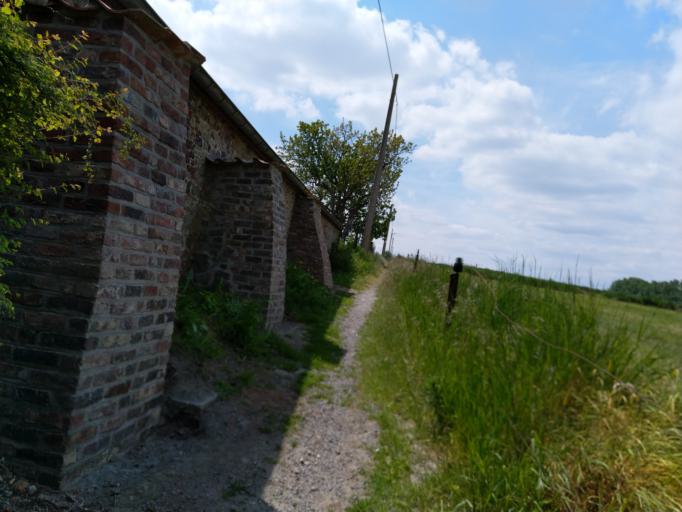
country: BE
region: Wallonia
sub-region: Province du Hainaut
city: Lens
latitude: 50.5570
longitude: 3.9170
